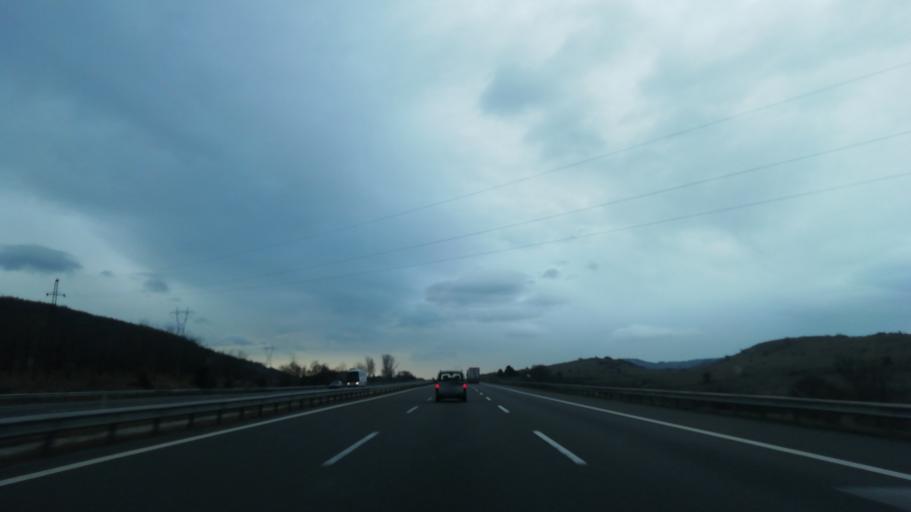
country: TR
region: Bolu
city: Yenicaga
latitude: 40.7621
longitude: 31.9915
